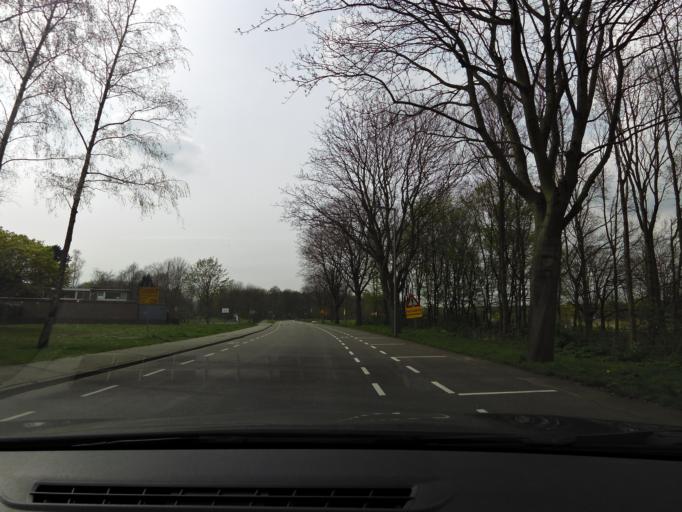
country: NL
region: South Holland
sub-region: Gemeente Spijkenisse
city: Spijkenisse
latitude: 51.8693
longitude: 4.3443
